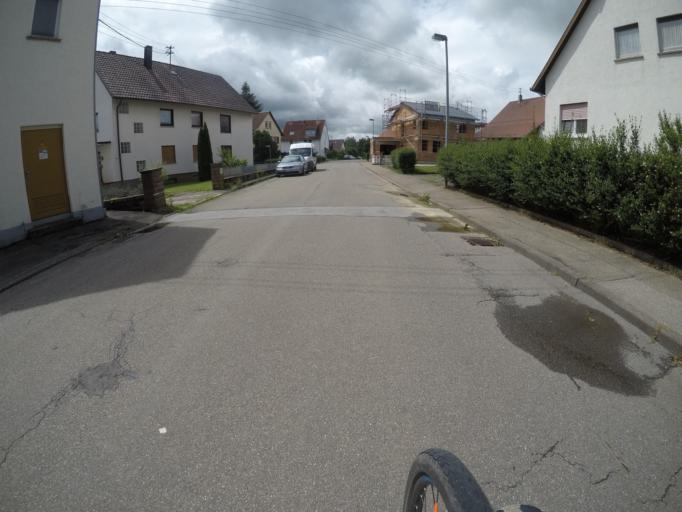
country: DE
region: Baden-Wuerttemberg
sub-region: Regierungsbezirk Stuttgart
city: Deckenpfronn
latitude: 48.6222
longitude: 8.8321
